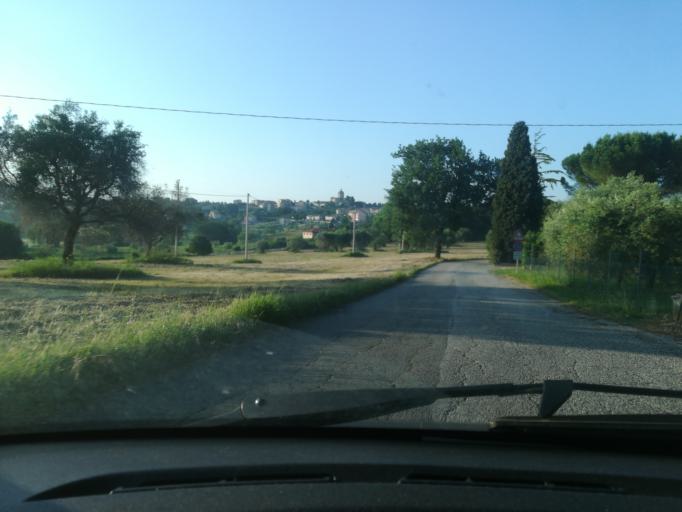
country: IT
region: The Marches
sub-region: Provincia di Macerata
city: Piediripa
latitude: 43.2837
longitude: 13.4706
